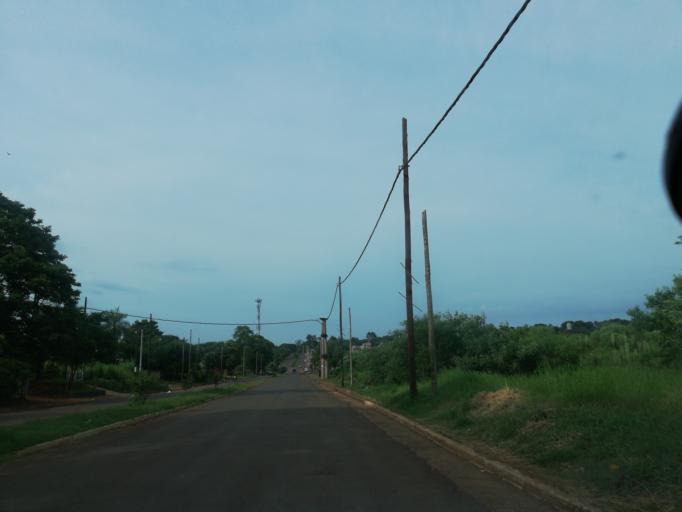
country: AR
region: Misiones
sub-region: Departamento de Capital
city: Posadas
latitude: -27.4129
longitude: -55.9173
